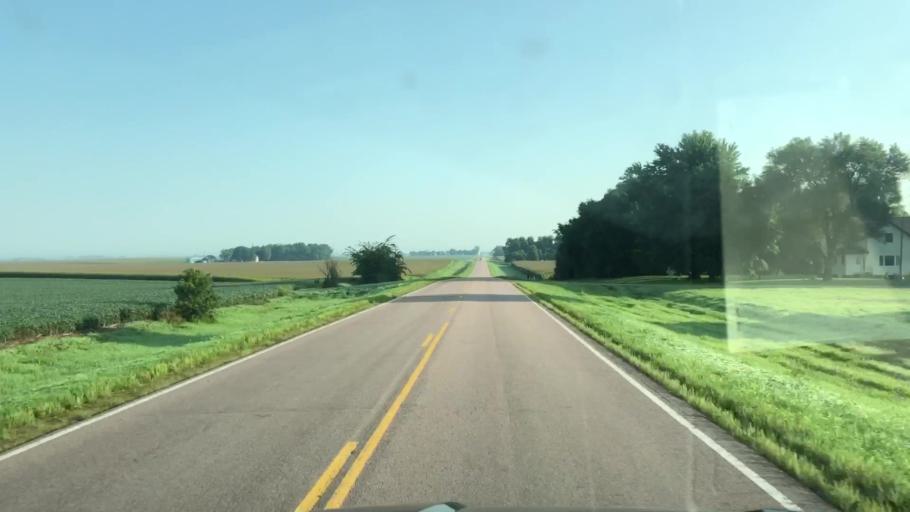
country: US
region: Iowa
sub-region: Lyon County
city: George
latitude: 43.2929
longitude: -95.9995
